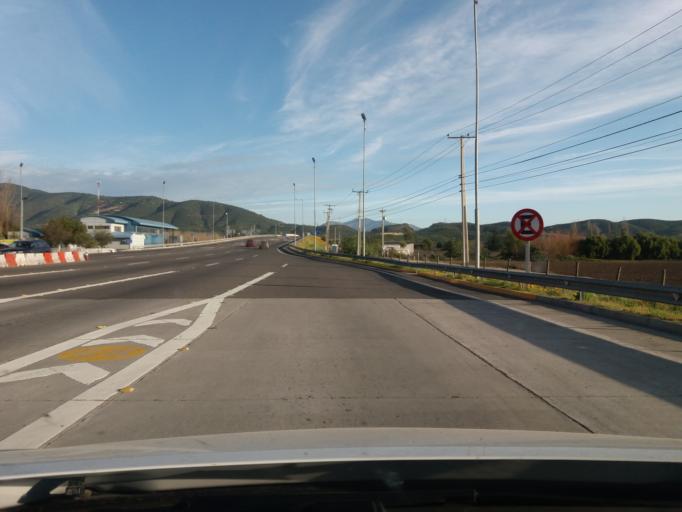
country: CL
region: Valparaiso
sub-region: Provincia de Quillota
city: Quillota
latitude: -32.9352
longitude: -71.2884
